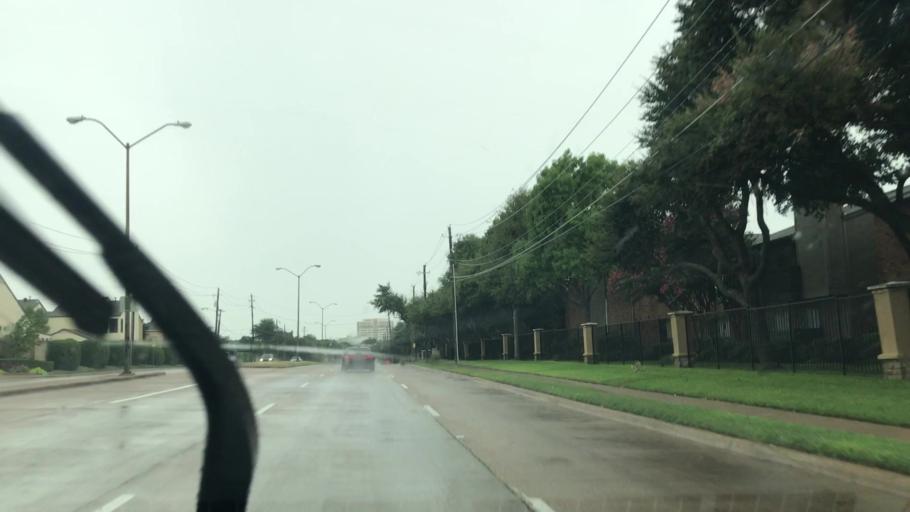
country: US
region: Texas
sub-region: Dallas County
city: Addison
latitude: 32.9388
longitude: -96.8054
